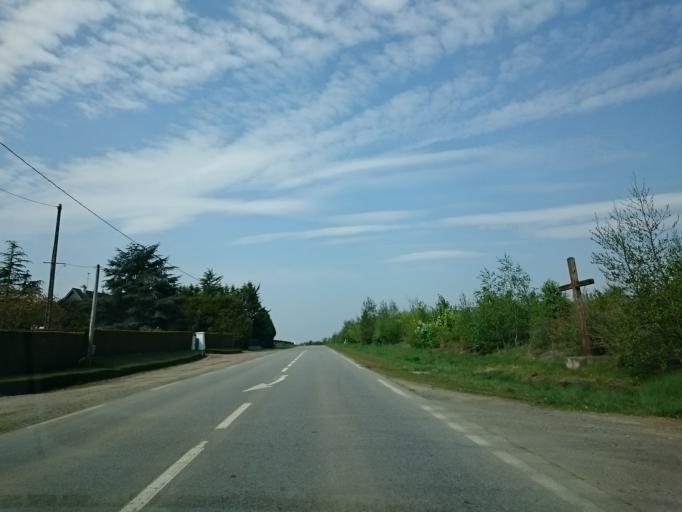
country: FR
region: Brittany
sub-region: Departement d'Ille-et-Vilaine
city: Saint-Armel
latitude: 48.0041
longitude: -1.5956
